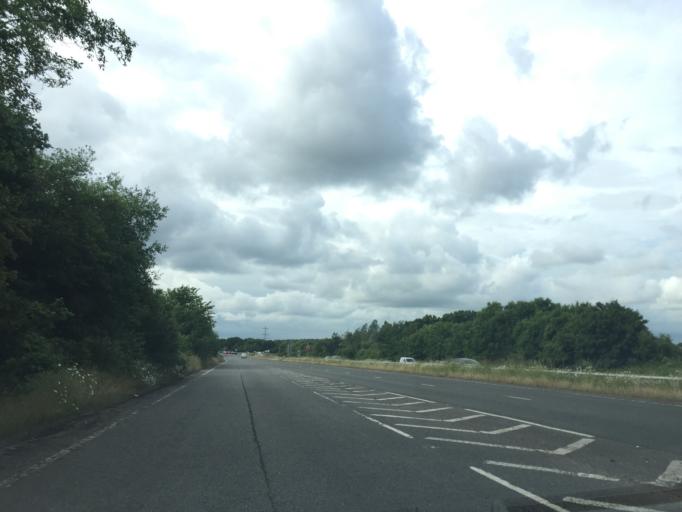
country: GB
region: England
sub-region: Hampshire
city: Totton
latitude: 50.9414
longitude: -1.5287
